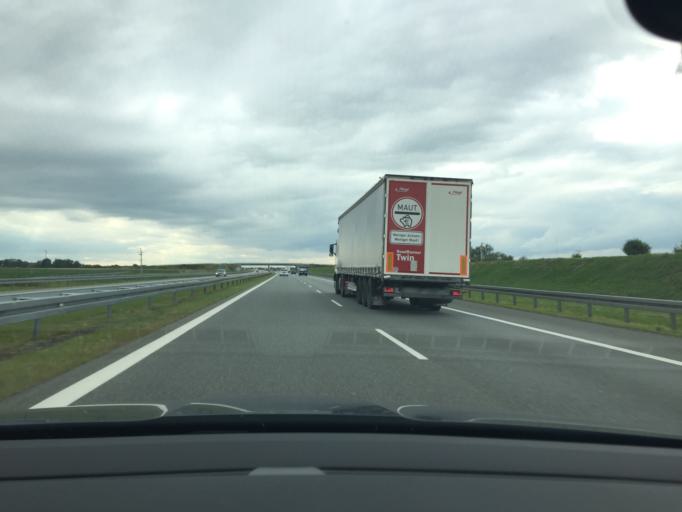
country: PL
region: Greater Poland Voivodeship
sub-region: Powiat szamotulski
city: Duszniki
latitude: 52.3899
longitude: 16.4362
